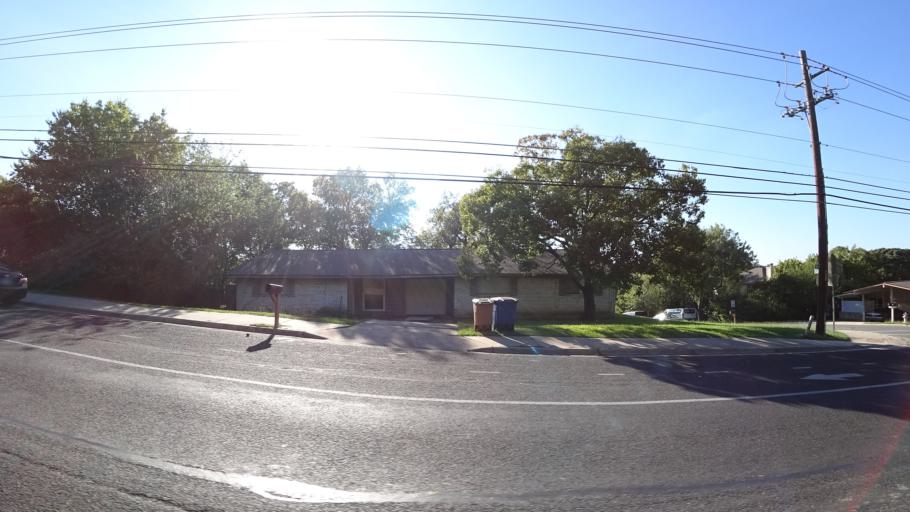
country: US
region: Texas
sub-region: Travis County
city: Austin
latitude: 30.2238
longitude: -97.7348
